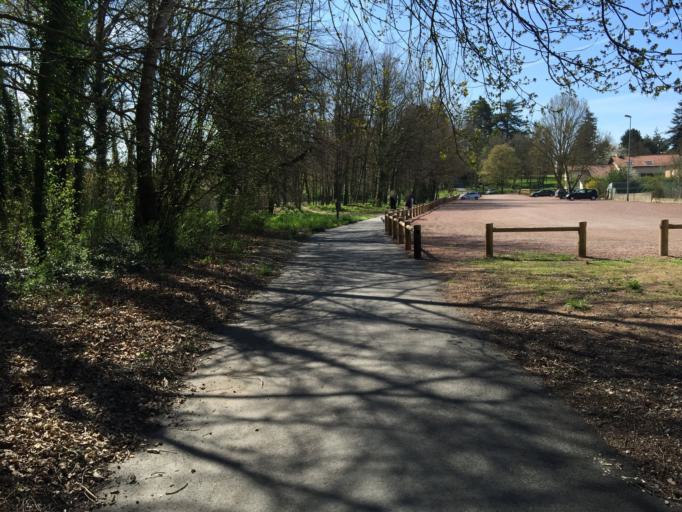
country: FR
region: Rhone-Alpes
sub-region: Departement de la Loire
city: Feurs
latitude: 45.7483
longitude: 4.2266
